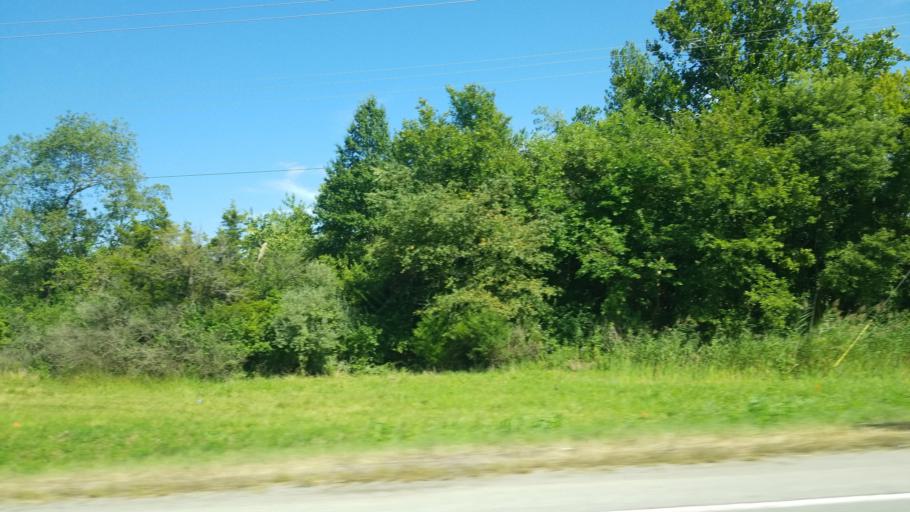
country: US
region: Illinois
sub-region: Williamson County
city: Marion
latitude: 37.7492
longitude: -88.9327
